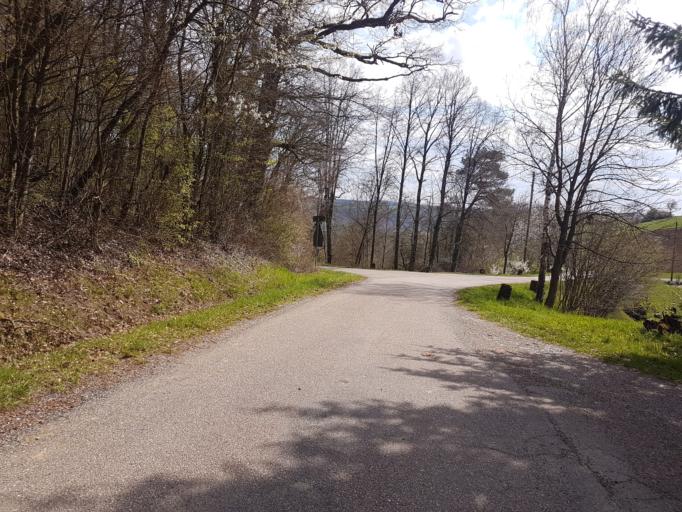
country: DE
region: Baden-Wuerttemberg
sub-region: Regierungsbezirk Stuttgart
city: Weissbach
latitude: 49.3603
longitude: 9.5660
